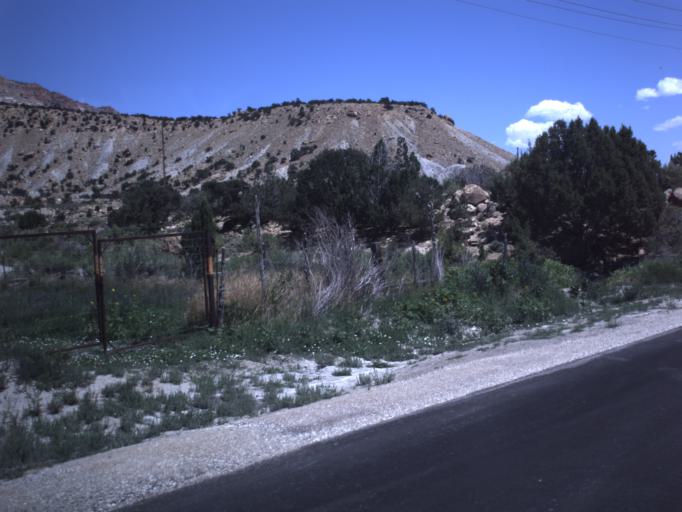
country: US
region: Utah
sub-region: Emery County
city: Orangeville
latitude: 39.2754
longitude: -111.1696
